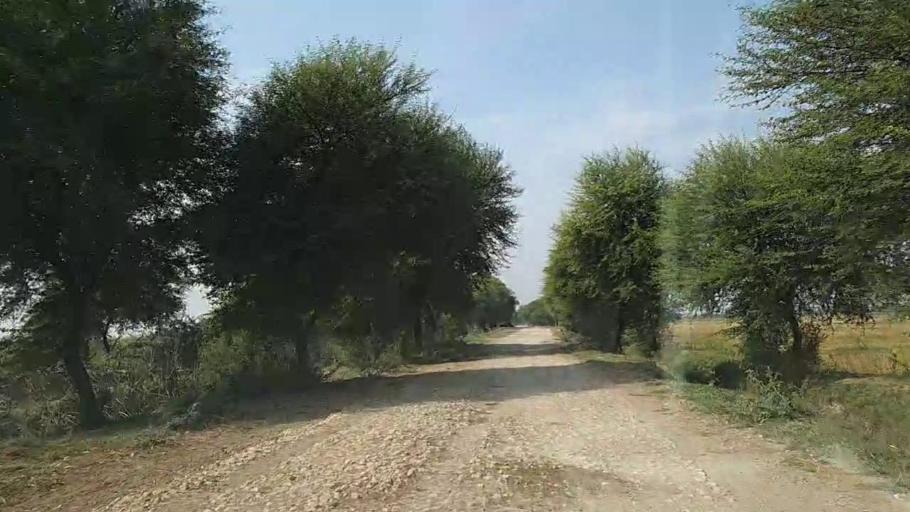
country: PK
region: Sindh
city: Mirpur Batoro
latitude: 24.6111
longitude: 68.2349
